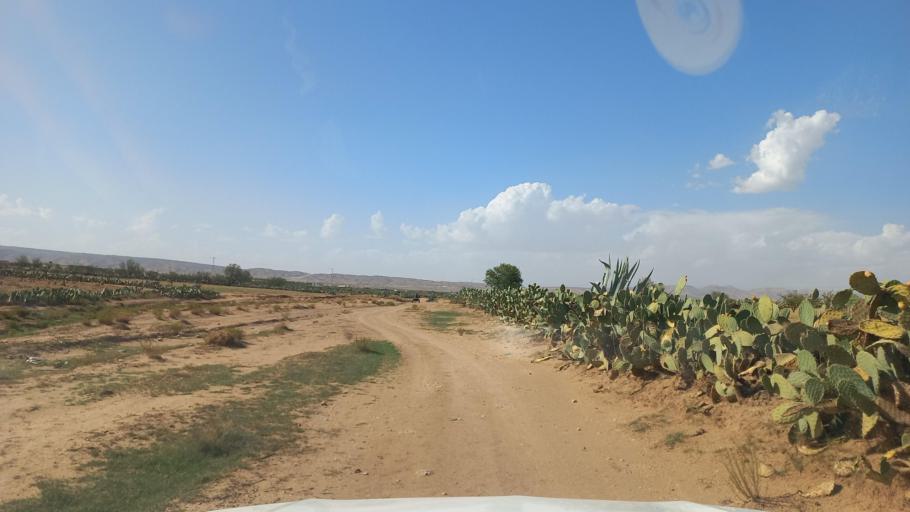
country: TN
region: Al Qasrayn
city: Sbiba
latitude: 35.3102
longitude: 9.0334
